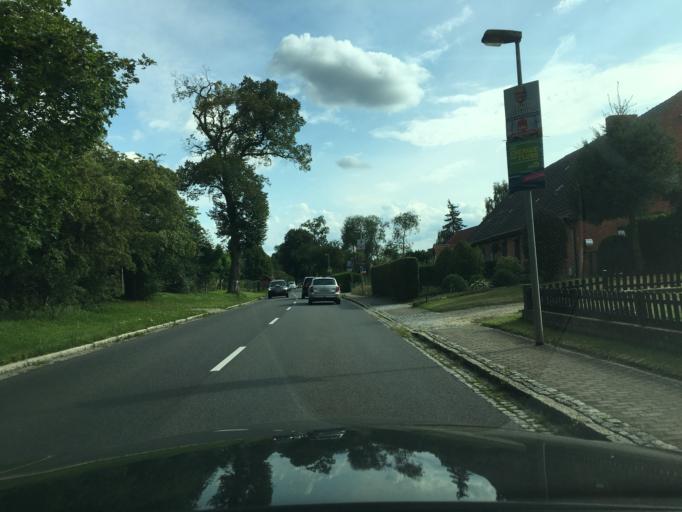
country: DE
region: Mecklenburg-Vorpommern
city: Neustrelitz
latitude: 53.4324
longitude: 13.0471
